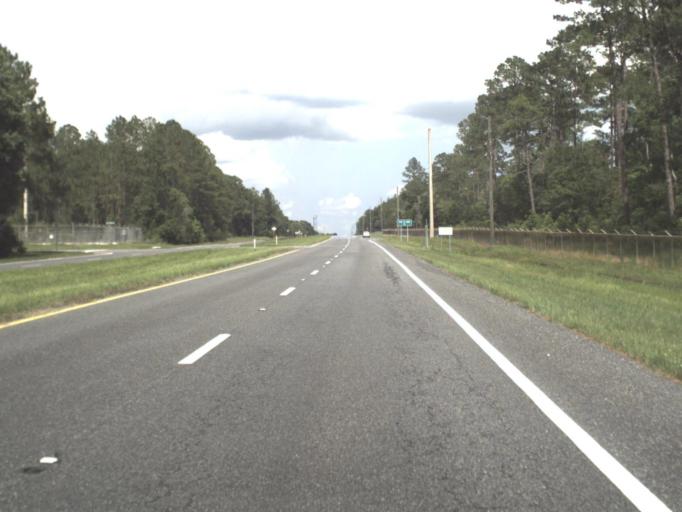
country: US
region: Florida
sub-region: Clay County
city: Middleburg
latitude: 29.9814
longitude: -81.9661
